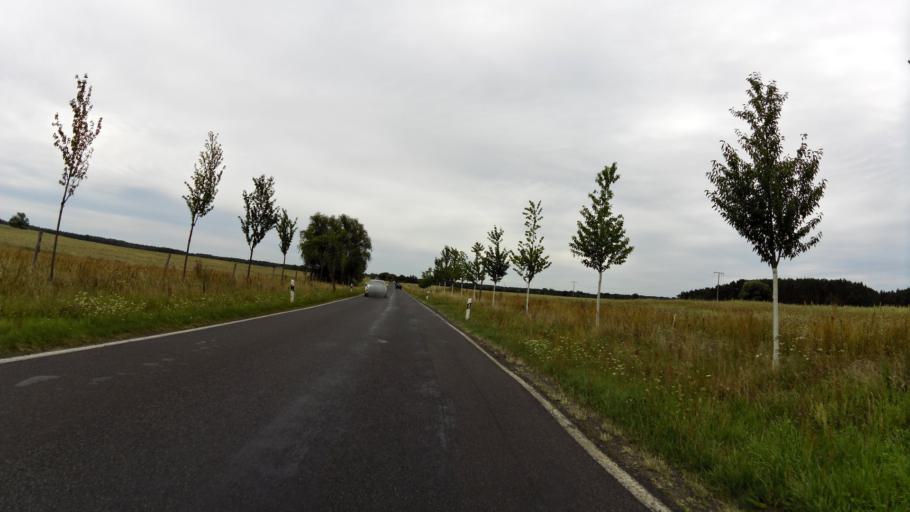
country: DE
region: Brandenburg
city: Wendisch Rietz
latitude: 52.1805
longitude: 14.0612
